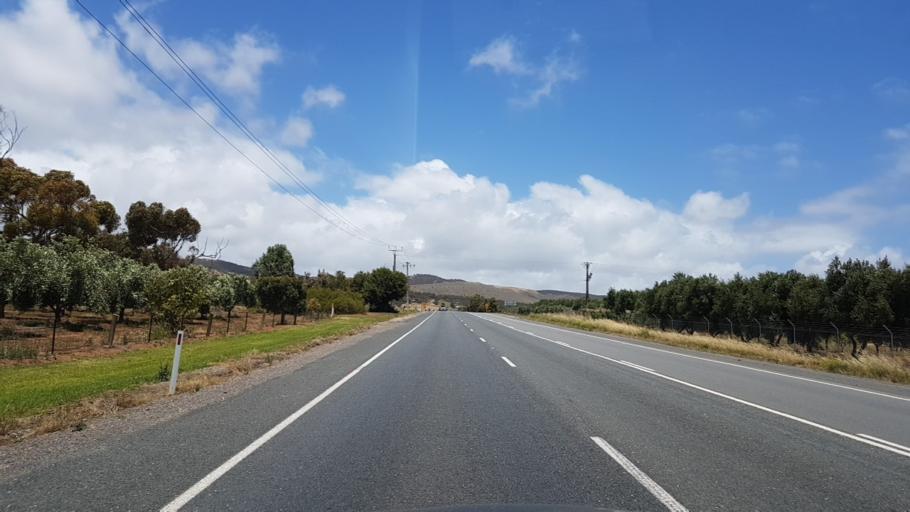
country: AU
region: South Australia
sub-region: Onkaparinga
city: Aldinga
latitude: -35.3171
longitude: 138.4741
